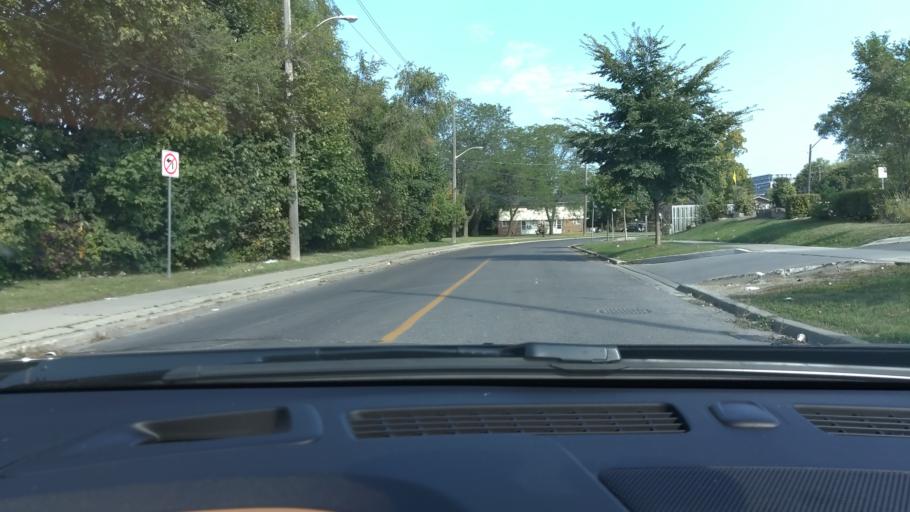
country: CA
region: Ontario
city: Toronto
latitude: 43.7175
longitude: -79.4489
